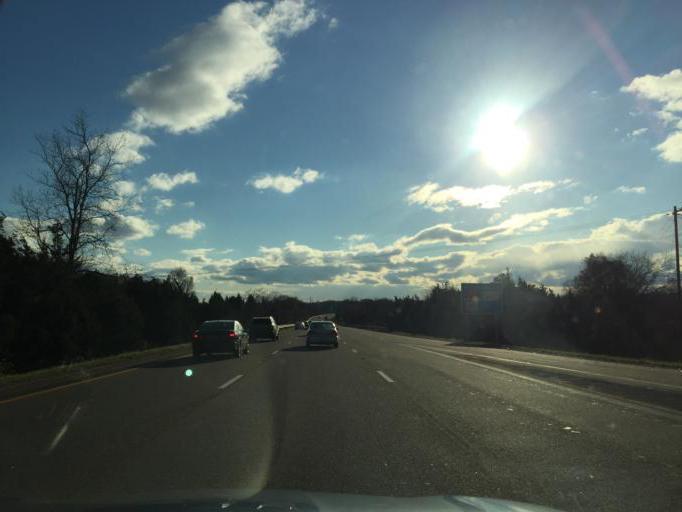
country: US
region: Massachusetts
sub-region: Bristol County
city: North Seekonk
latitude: 41.9153
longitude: -71.3355
